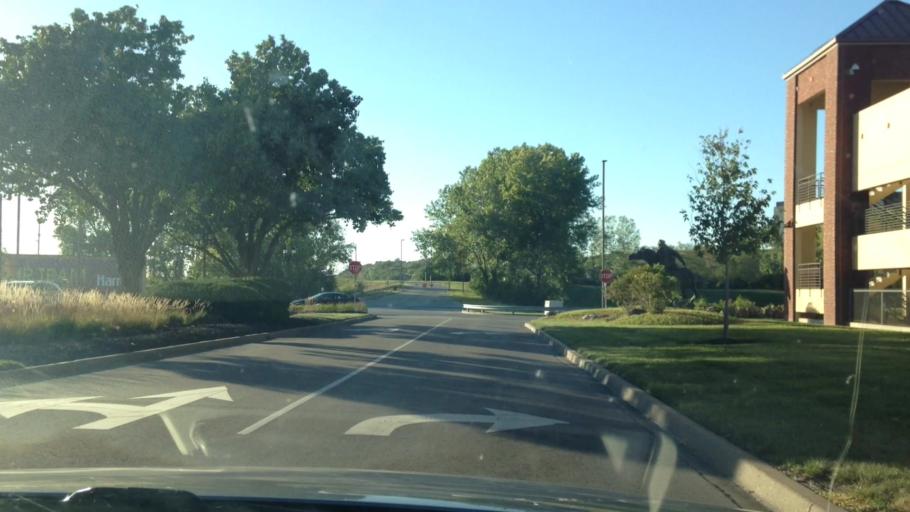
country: US
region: Missouri
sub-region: Clay County
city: North Kansas City
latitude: 39.1433
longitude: -94.5458
